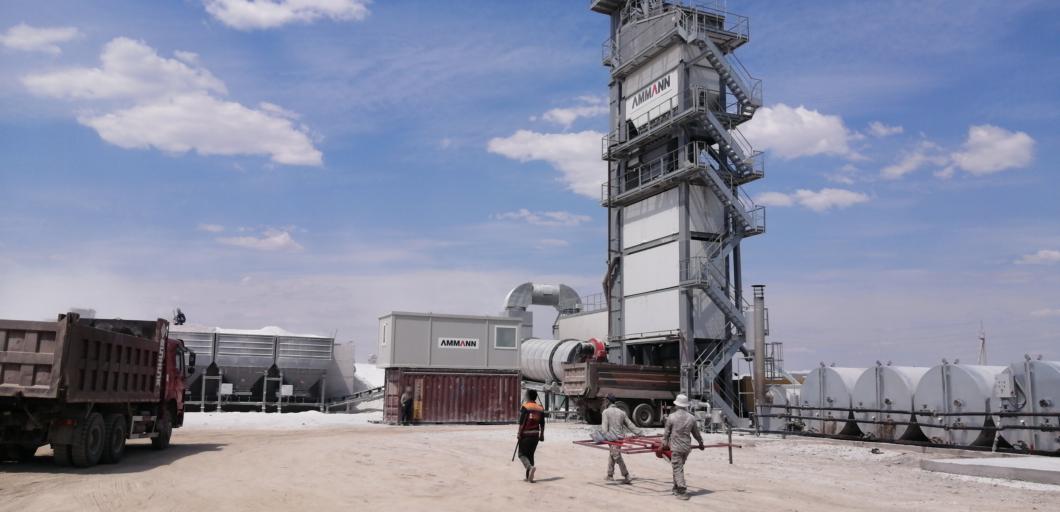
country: KZ
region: Qaraghandy
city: Balqash
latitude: 46.6272
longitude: 74.3759
